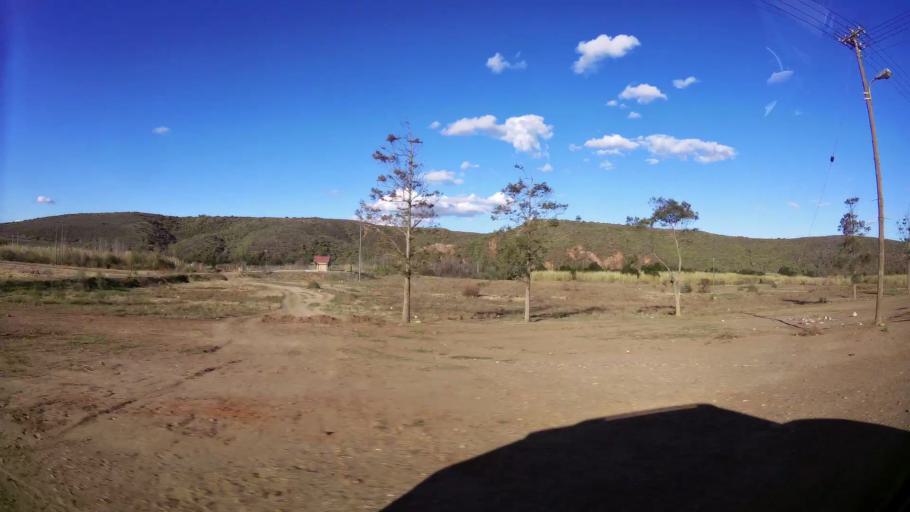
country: ZA
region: Western Cape
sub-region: Eden District Municipality
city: Riversdale
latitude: -34.1040
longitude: 20.9699
